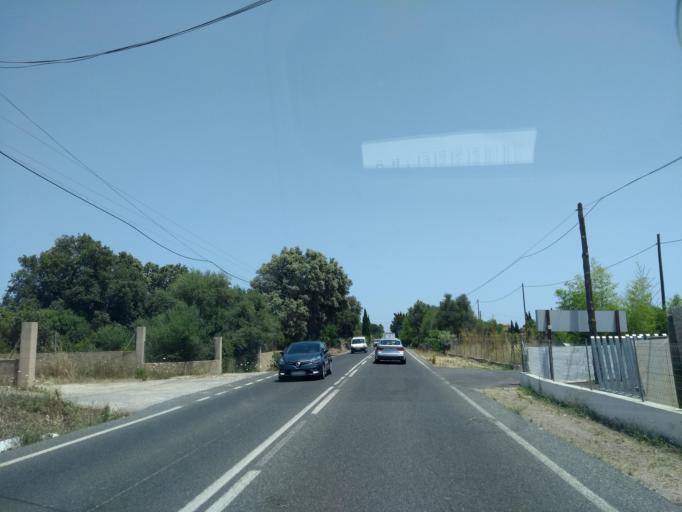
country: ES
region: Balearic Islands
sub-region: Illes Balears
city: Inca
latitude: 39.7304
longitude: 2.9306
